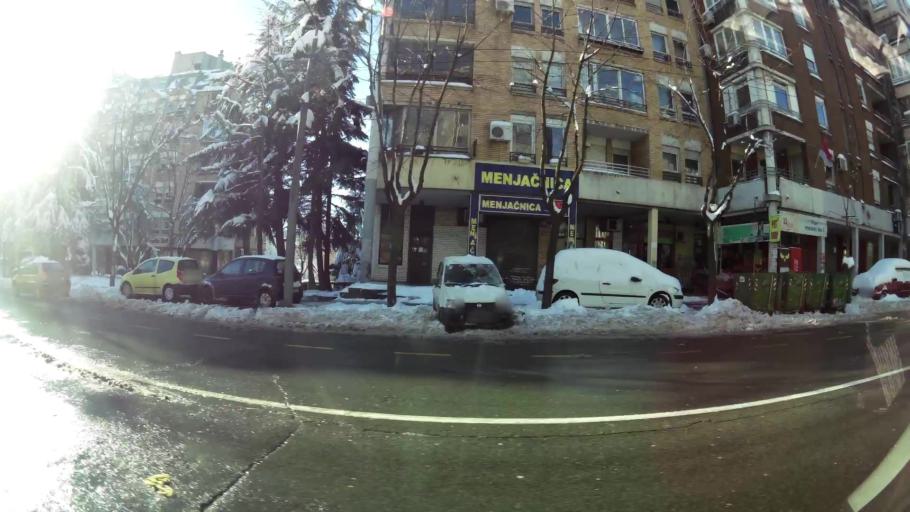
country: RS
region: Central Serbia
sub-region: Belgrade
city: Vracar
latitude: 44.7930
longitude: 20.4951
